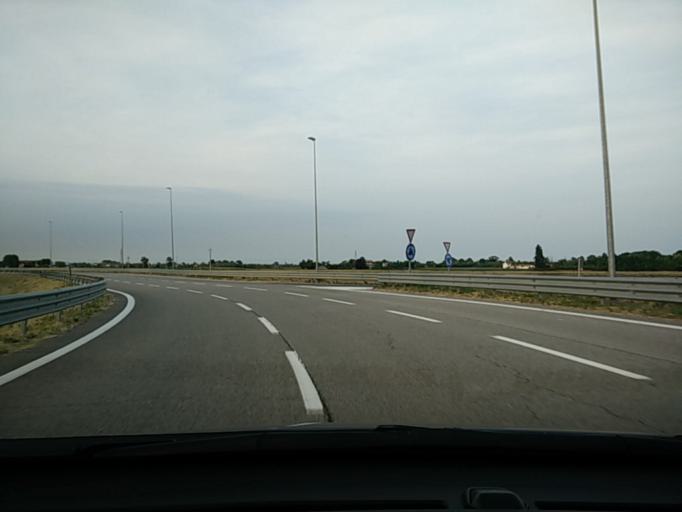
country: IT
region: Veneto
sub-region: Provincia di Venezia
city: Musile di Piave
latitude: 45.5907
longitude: 12.5549
